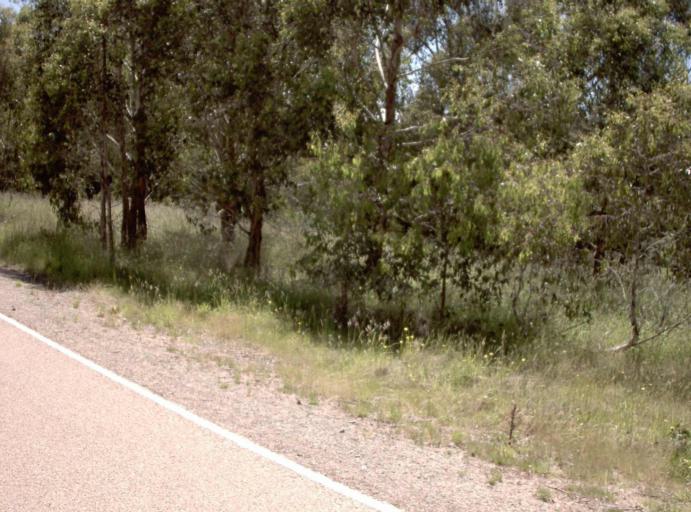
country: AU
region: Victoria
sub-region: East Gippsland
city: Lakes Entrance
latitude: -37.2121
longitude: 148.2689
